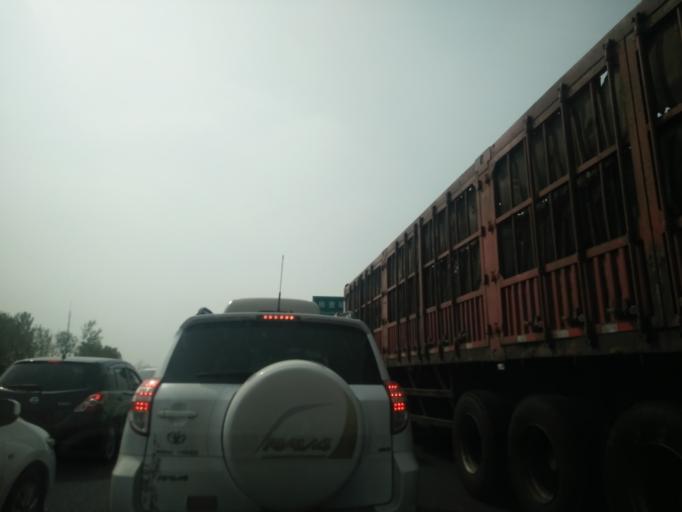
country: CN
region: Beijing
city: Xiji
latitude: 39.7988
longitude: 116.9048
